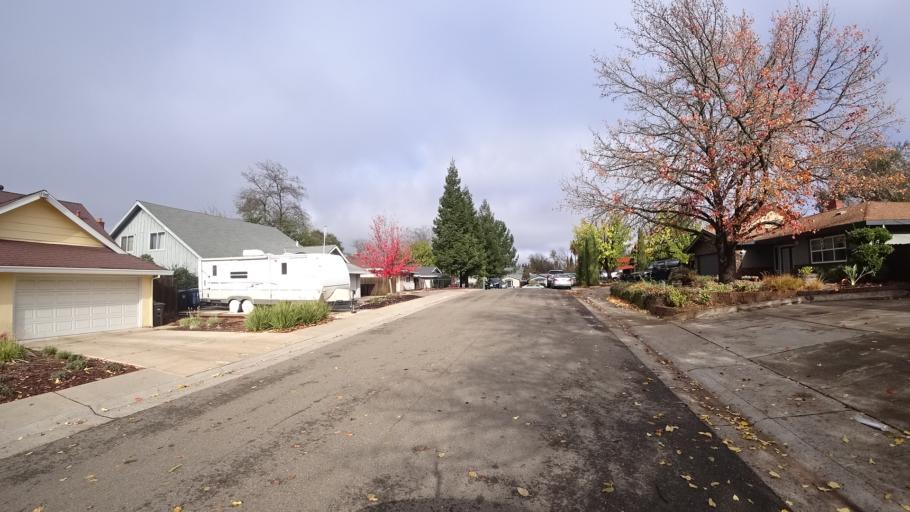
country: US
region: California
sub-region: Sacramento County
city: Antelope
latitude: 38.6958
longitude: -121.3068
